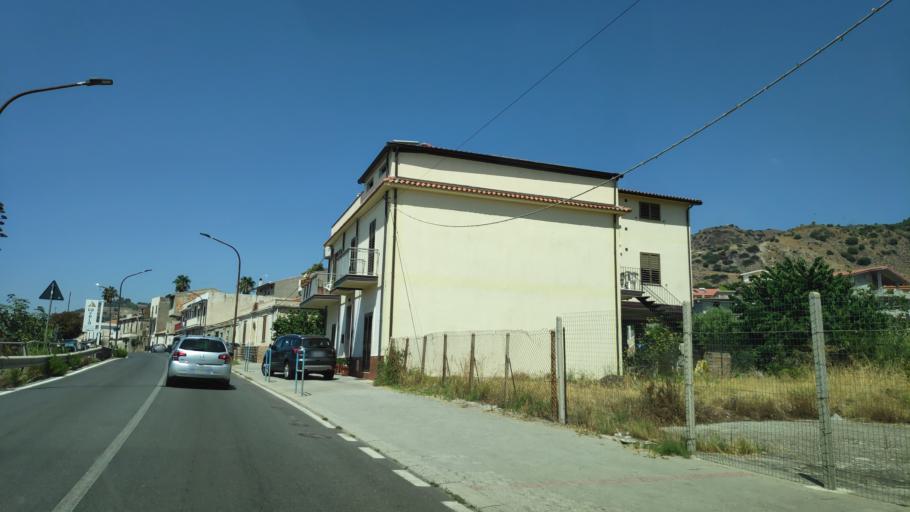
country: IT
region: Calabria
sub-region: Provincia di Reggio Calabria
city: Palizzi Marina
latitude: 37.9182
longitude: 15.9939
